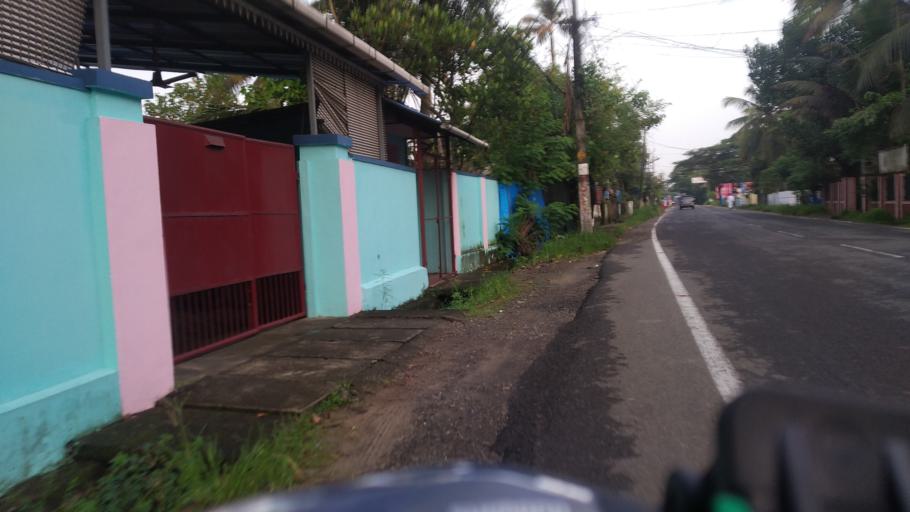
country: IN
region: Kerala
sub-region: Ernakulam
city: Cochin
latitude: 10.0017
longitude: 76.2342
